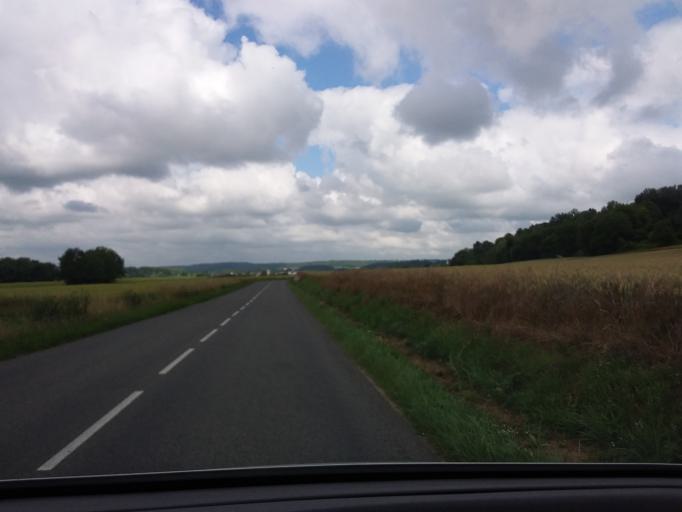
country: FR
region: Picardie
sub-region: Departement de l'Aisne
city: Vailly-sur-Aisne
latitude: 49.4046
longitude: 3.5435
